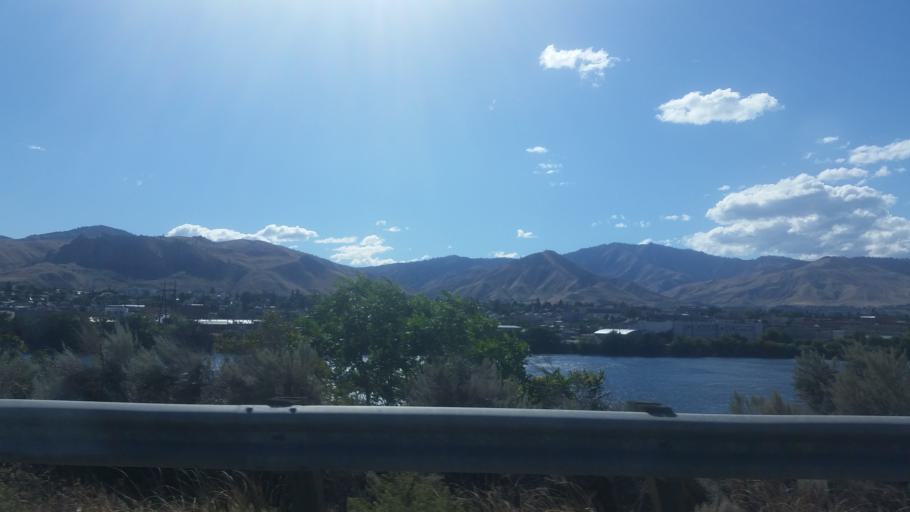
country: US
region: Washington
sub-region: Douglas County
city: East Wenatchee
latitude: 47.4210
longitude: -120.2971
